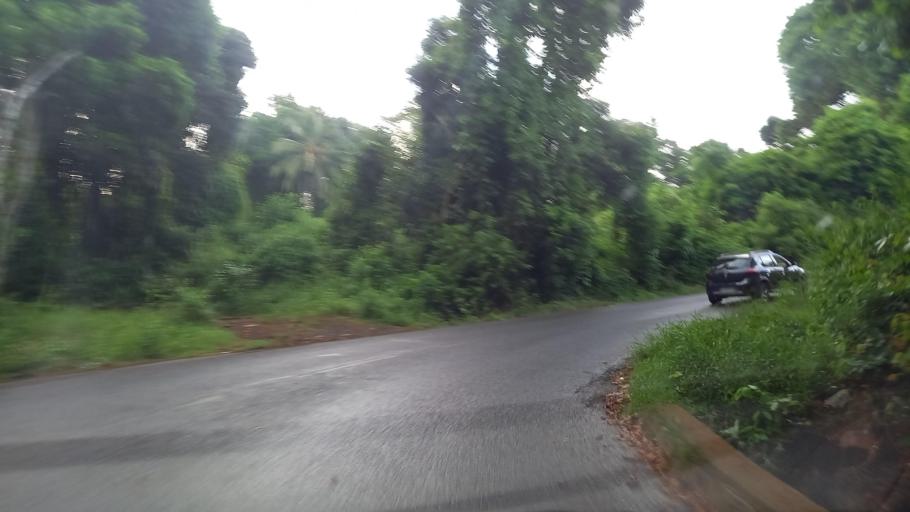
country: YT
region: Dembeni
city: Dembeni
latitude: -12.8416
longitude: 45.1661
